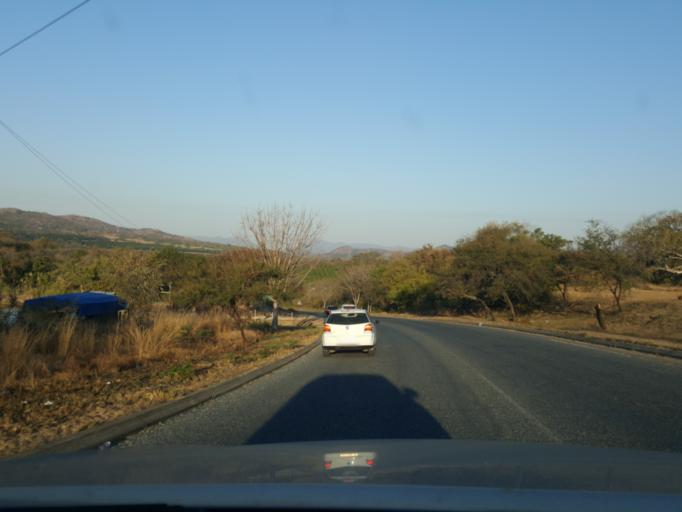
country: ZA
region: Mpumalanga
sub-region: Ehlanzeni District
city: Nelspruit
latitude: -25.4455
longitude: 31.0134
